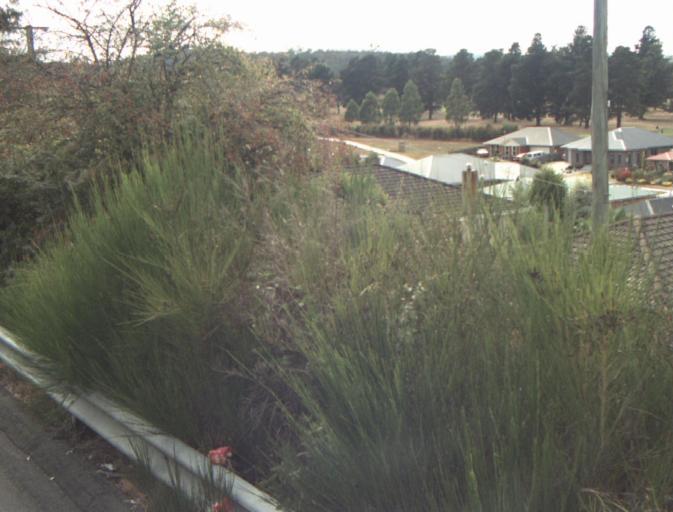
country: AU
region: Tasmania
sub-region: Launceston
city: Invermay
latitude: -41.3937
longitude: 147.1326
